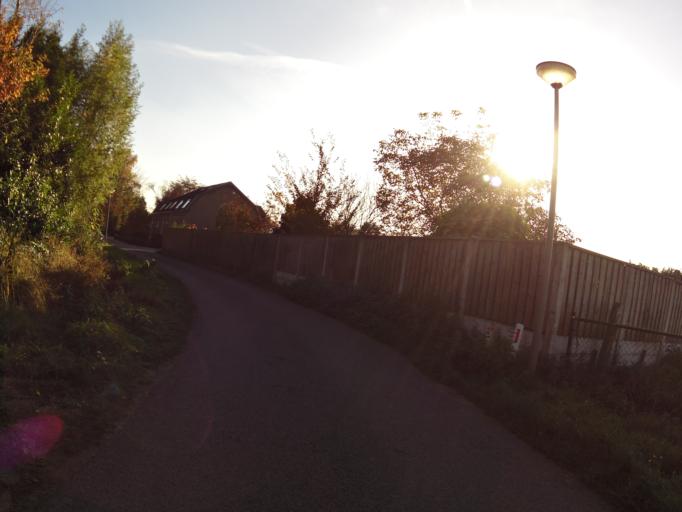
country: NL
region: North Brabant
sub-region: Gemeente Boxtel
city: Boxtel
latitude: 51.5871
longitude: 5.3084
